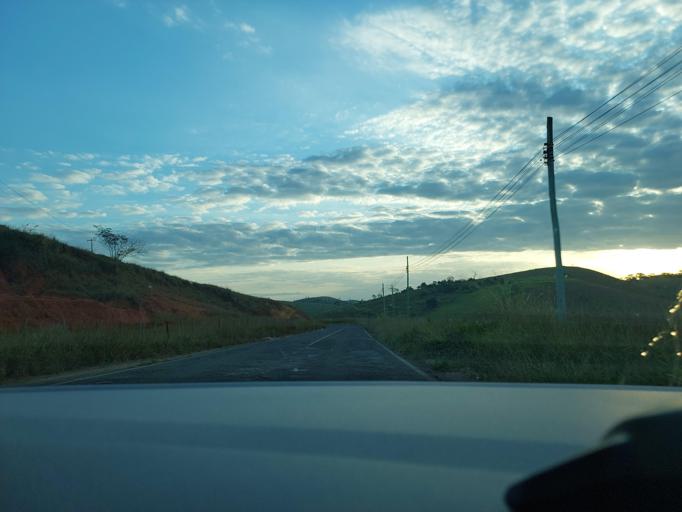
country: BR
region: Rio de Janeiro
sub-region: Natividade
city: Natividade
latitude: -21.1924
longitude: -42.1139
